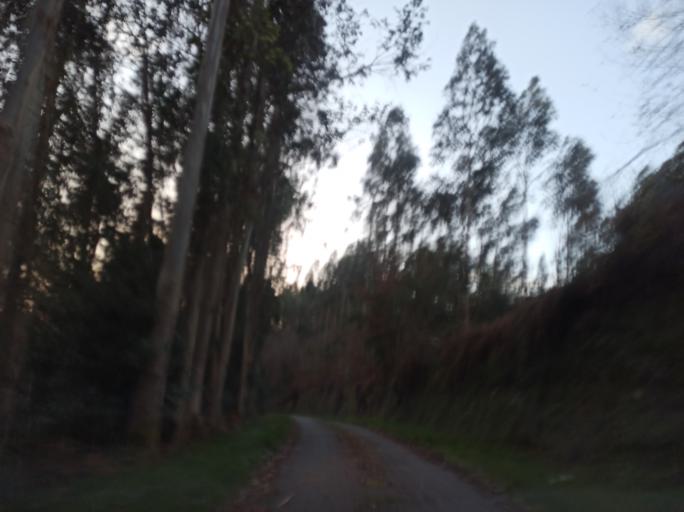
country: ES
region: Galicia
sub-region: Provincia da Coruna
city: Cesuras
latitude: 43.1770
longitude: -8.1631
